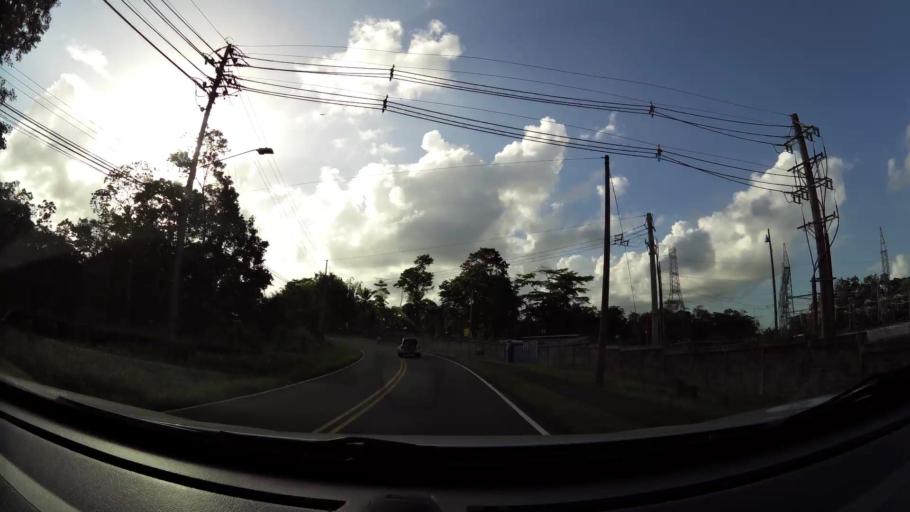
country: CR
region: Limon
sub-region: Canton de Siquirres
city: Siquirres
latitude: 10.0978
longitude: -83.5257
